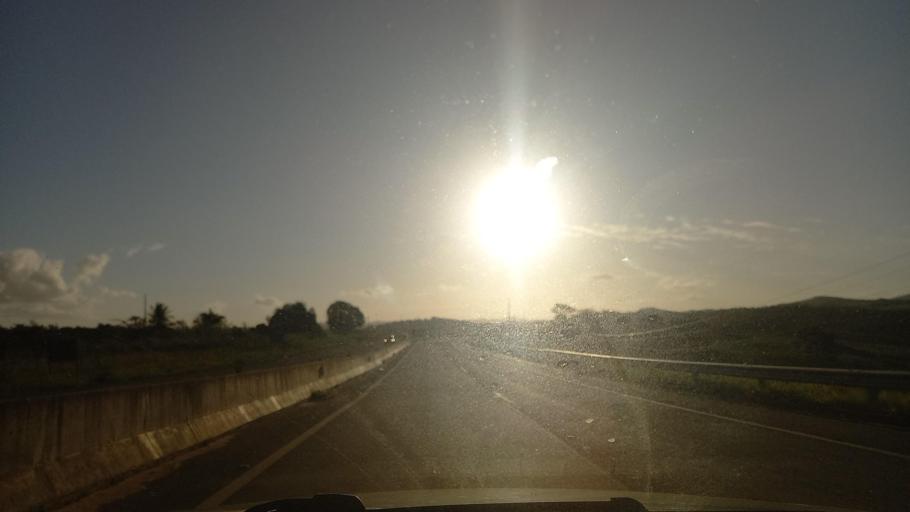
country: BR
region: Alagoas
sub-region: Limoeiro De Anadia
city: Limoeiro de Anadia
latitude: -9.7400
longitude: -36.4816
